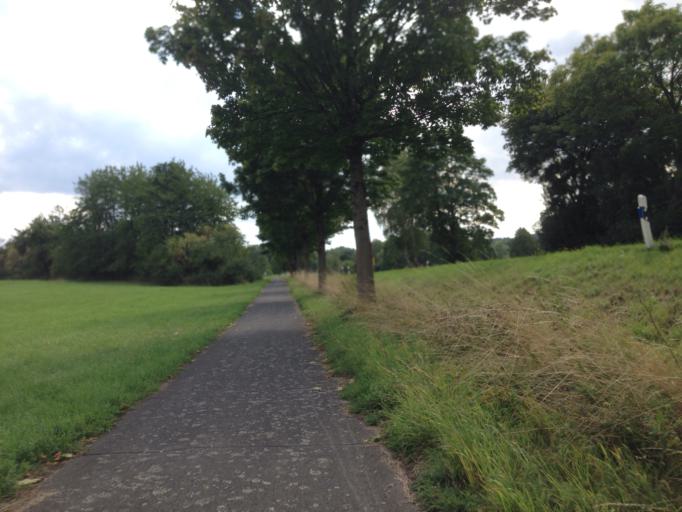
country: DE
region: Hesse
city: Mengerskirchen
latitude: 50.5499
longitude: 8.1531
